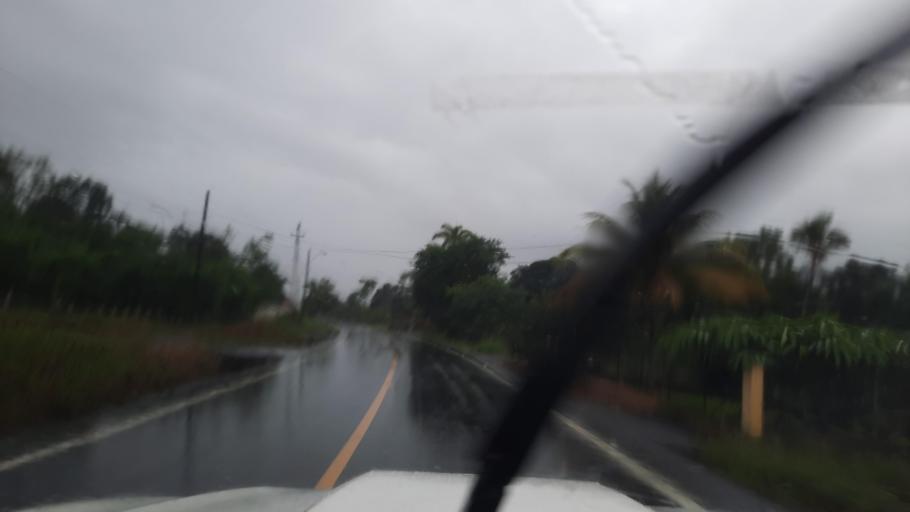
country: PA
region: Chiriqui
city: Sortova
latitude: 8.5788
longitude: -82.6372
